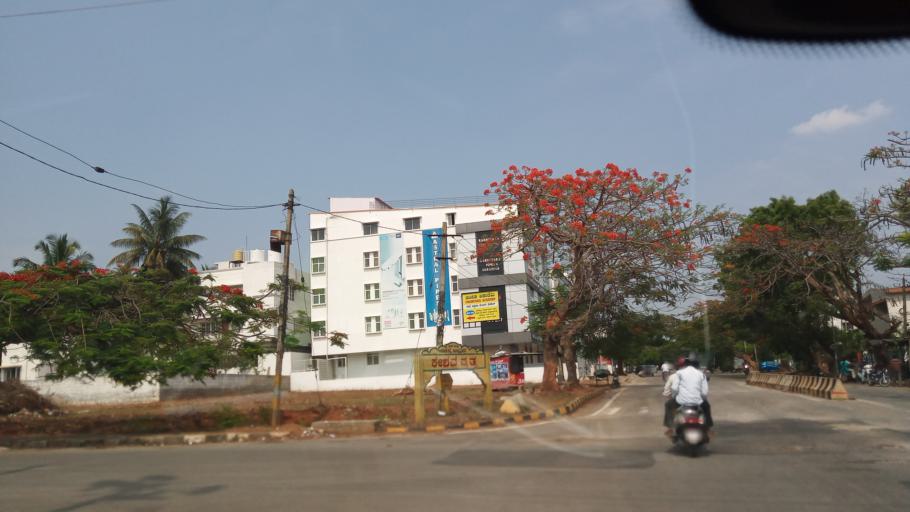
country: IN
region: Karnataka
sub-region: Mysore
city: Mysore
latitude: 12.2872
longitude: 76.6194
